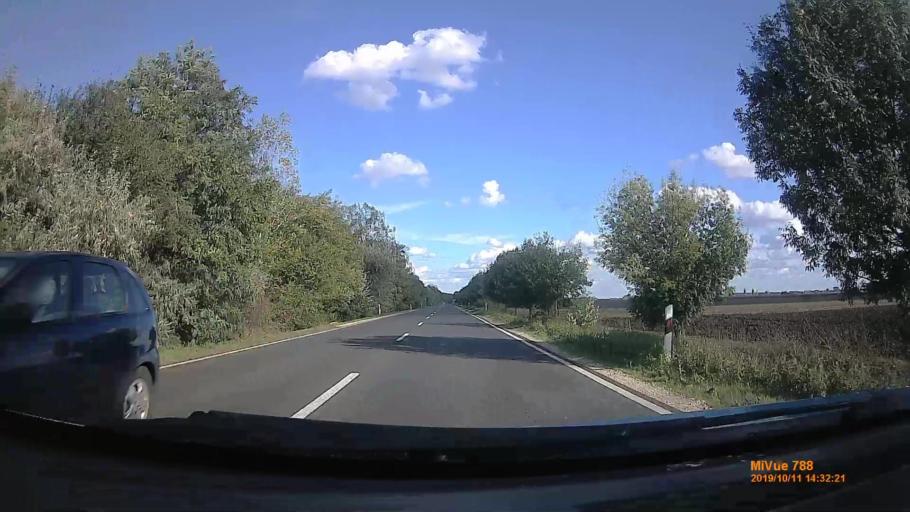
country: HU
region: Hajdu-Bihar
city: Balmazujvaros
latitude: 47.5621
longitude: 21.4361
